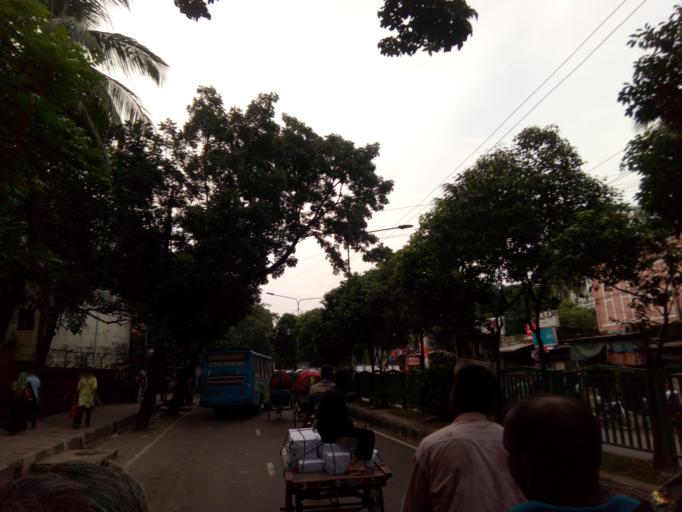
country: BD
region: Dhaka
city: Azimpur
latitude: 23.7261
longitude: 90.3865
